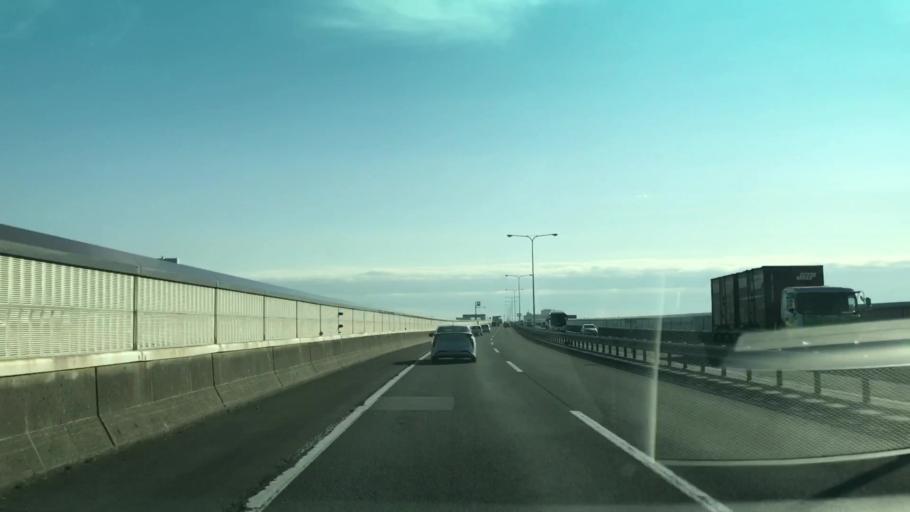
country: JP
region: Hokkaido
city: Sapporo
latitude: 43.1032
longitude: 141.3792
